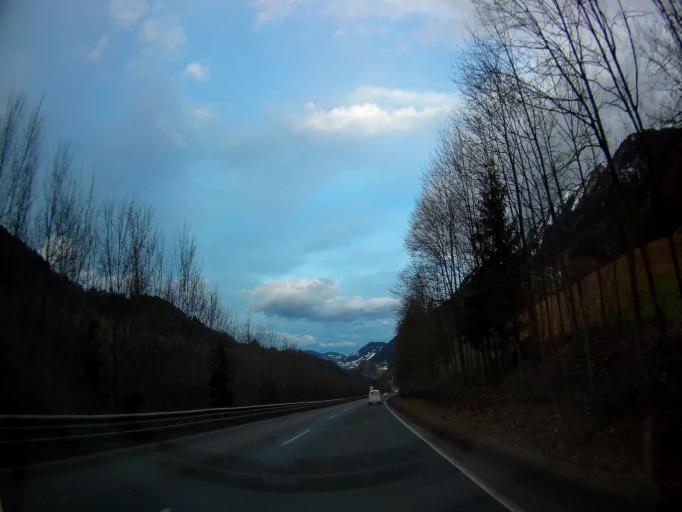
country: AT
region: Salzburg
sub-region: Politischer Bezirk Zell am See
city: Lend
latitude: 47.2959
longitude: 13.0665
